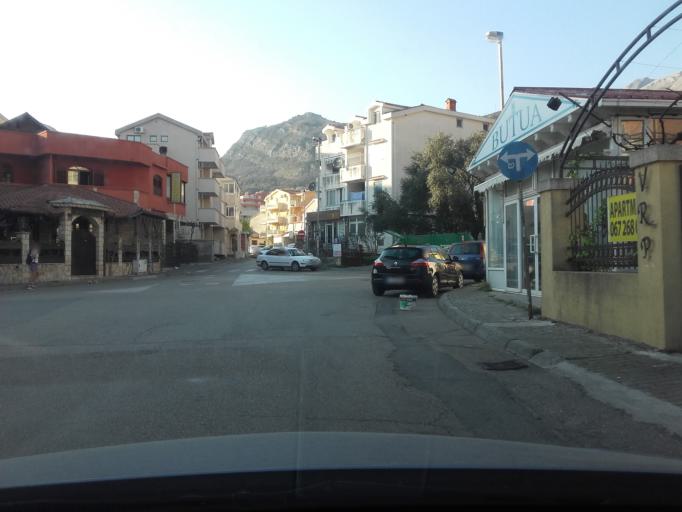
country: ME
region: Budva
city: Budva
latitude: 42.2910
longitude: 18.8472
